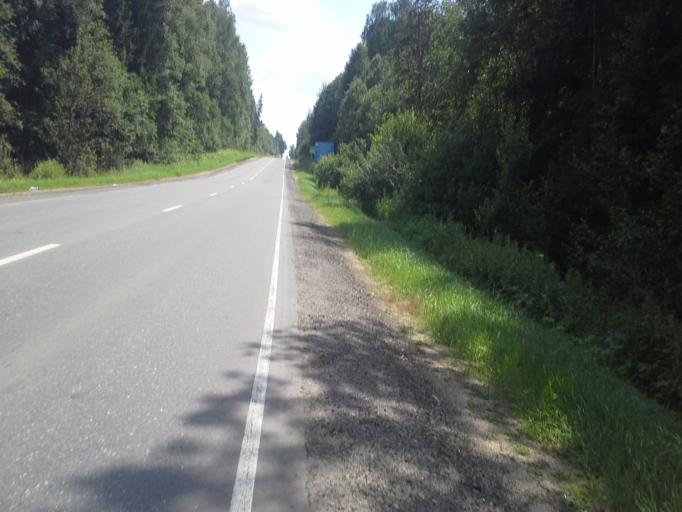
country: RU
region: Moskovskaya
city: Chupryakovo
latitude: 55.4802
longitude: 36.6911
